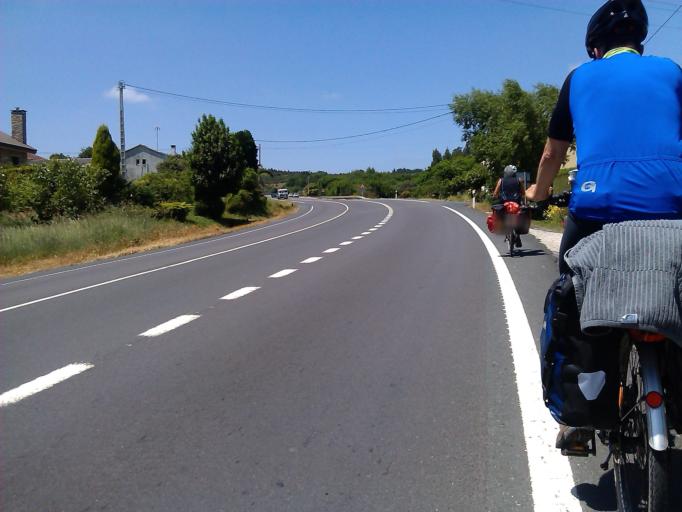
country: ES
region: Galicia
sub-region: Provincia da Coruna
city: Oroso
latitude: 42.9086
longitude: -8.3989
